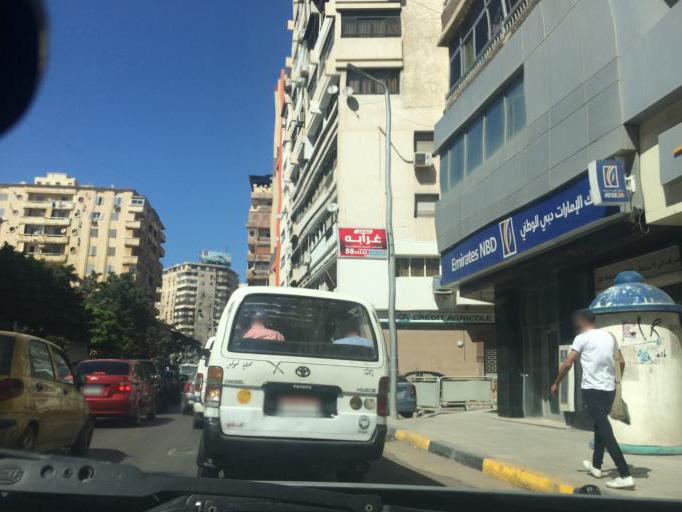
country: EG
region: Alexandria
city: Alexandria
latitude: 31.2366
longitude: 29.9610
